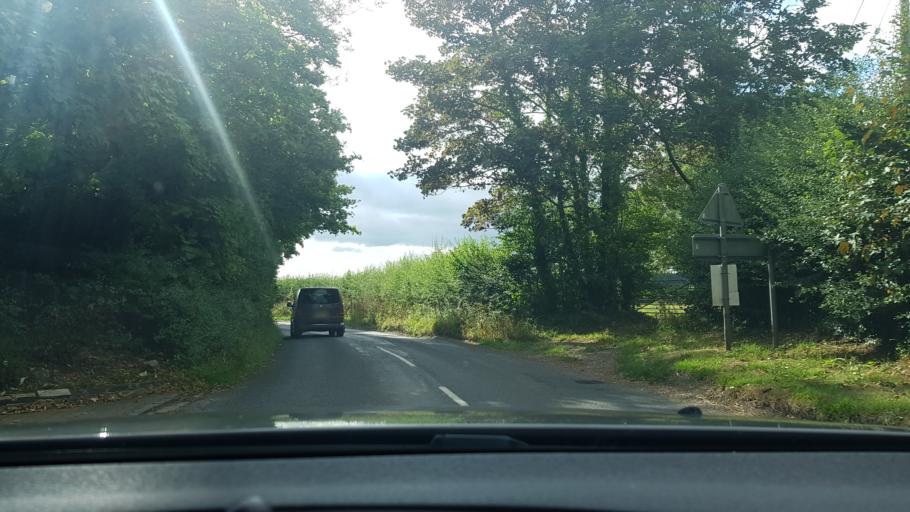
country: GB
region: England
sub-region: West Berkshire
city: Hermitage
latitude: 51.4663
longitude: -1.2078
